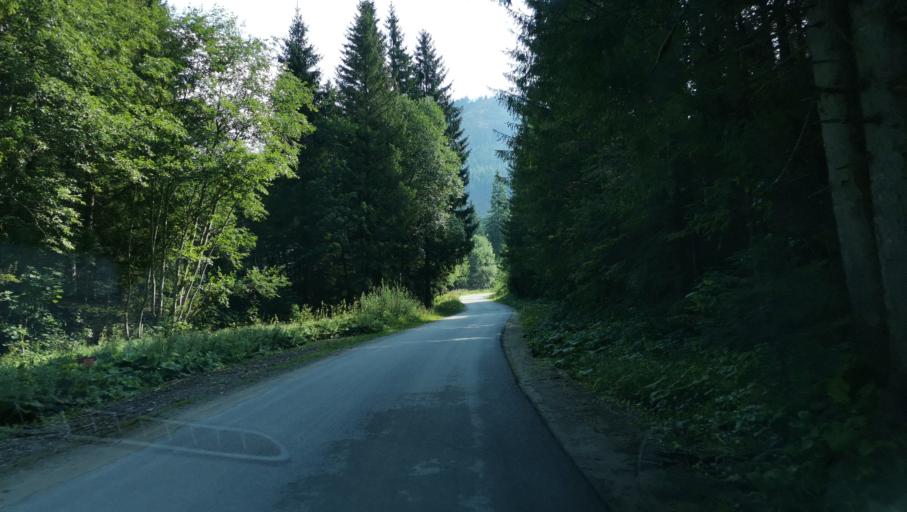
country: AT
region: Styria
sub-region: Politischer Bezirk Liezen
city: Trieben
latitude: 47.5262
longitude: 14.4807
